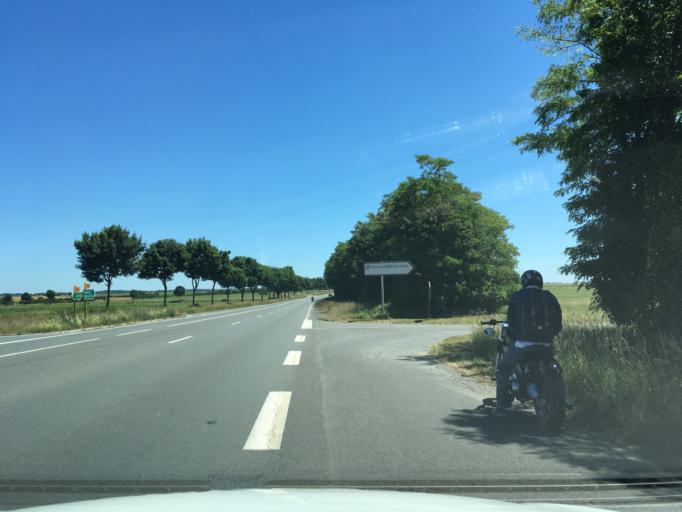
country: FR
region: Poitou-Charentes
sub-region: Departement des Deux-Sevres
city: Vouille
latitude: 46.3182
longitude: -0.3998
